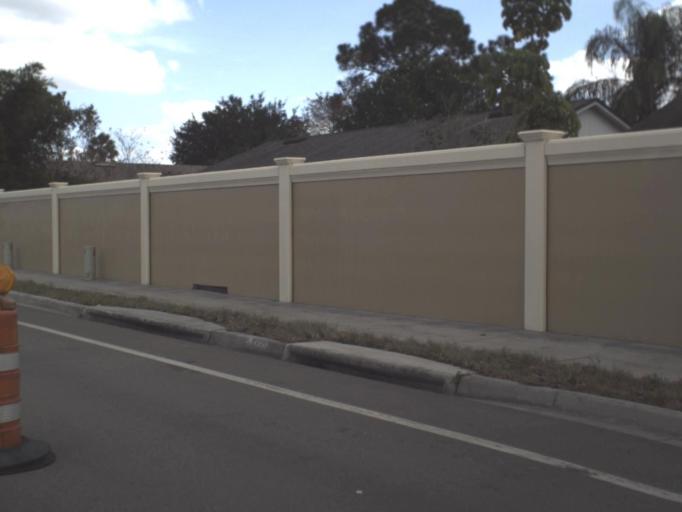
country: US
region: Florida
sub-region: Osceola County
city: Buenaventura Lakes
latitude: 28.3441
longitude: -81.3741
